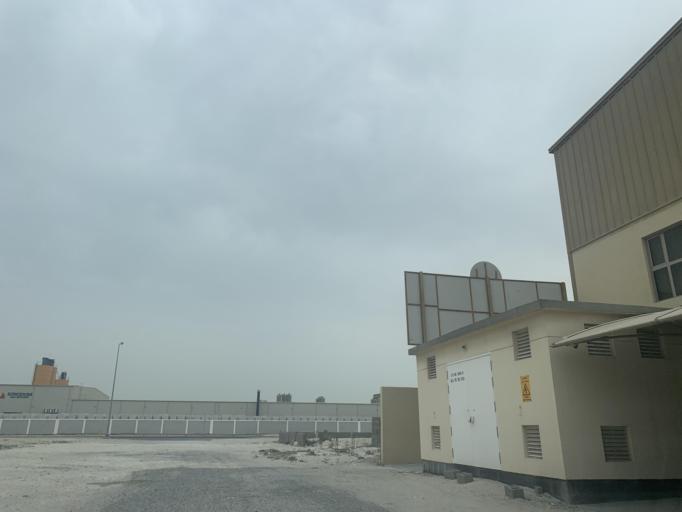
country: BH
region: Muharraq
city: Al Hadd
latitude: 26.2123
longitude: 50.6629
